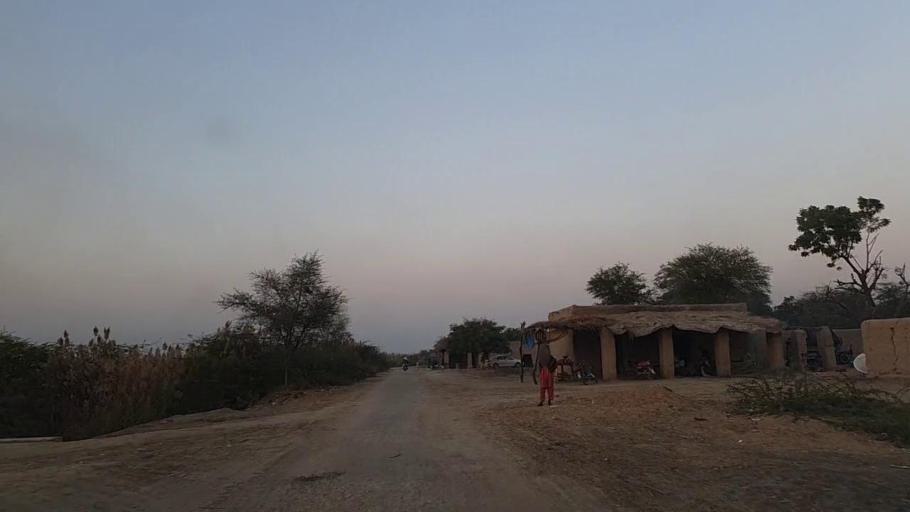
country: PK
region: Sindh
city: Bandhi
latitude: 26.6015
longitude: 68.3651
